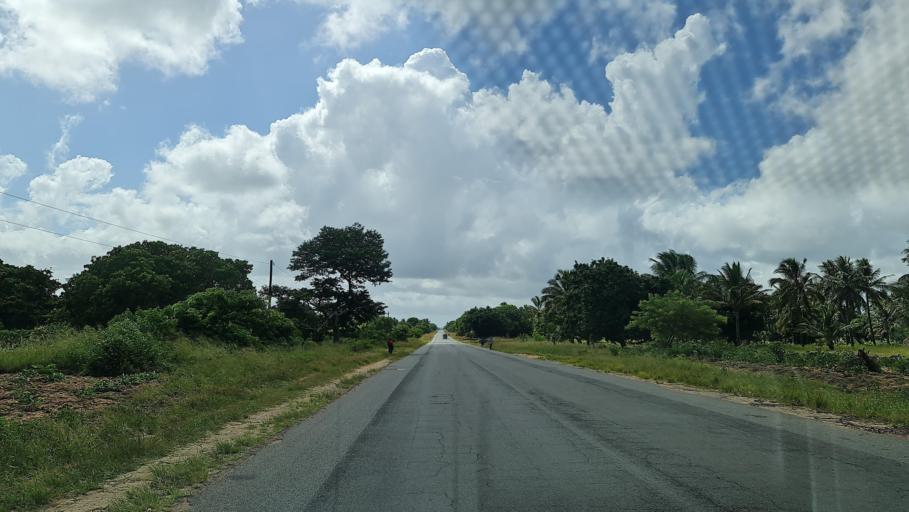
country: MZ
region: Gaza
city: Manjacaze
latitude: -24.6766
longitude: 34.5886
